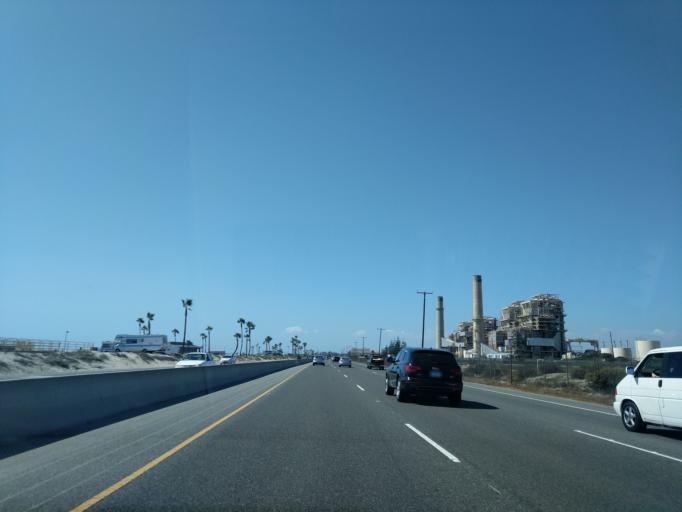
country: US
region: California
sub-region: Orange County
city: Huntington Beach
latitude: 33.6412
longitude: -117.9757
